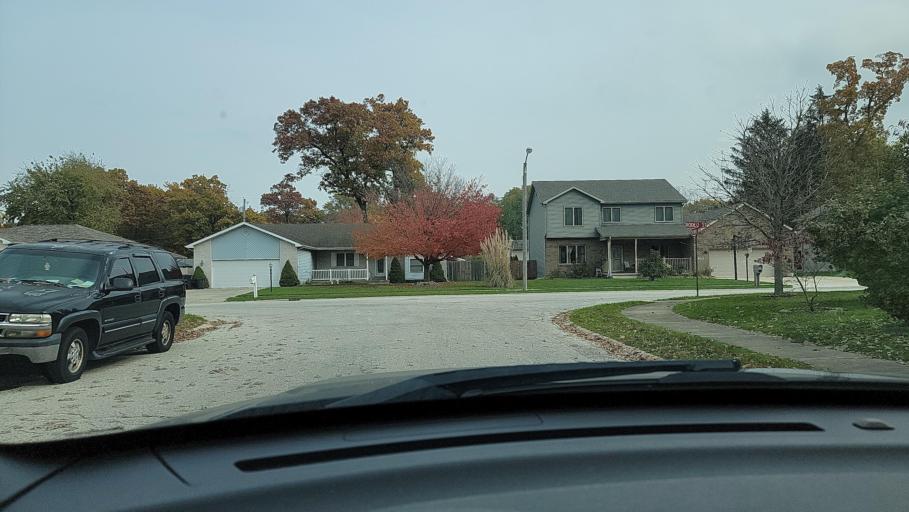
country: US
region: Indiana
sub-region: Porter County
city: Portage
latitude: 41.5856
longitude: -87.1571
